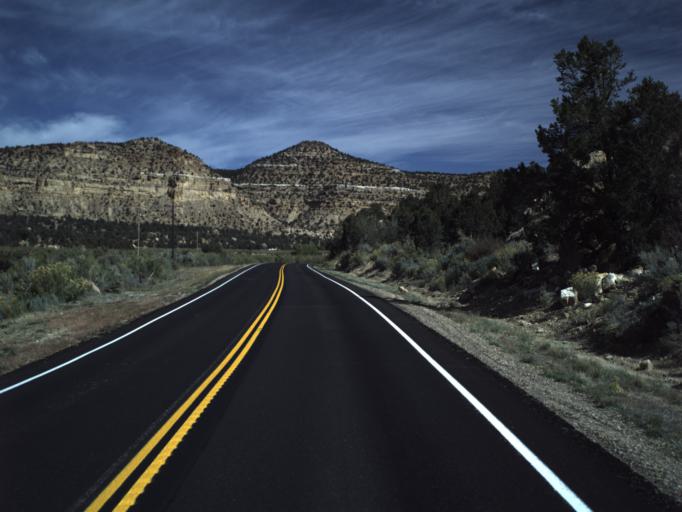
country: US
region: Utah
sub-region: Wayne County
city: Loa
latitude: 37.7521
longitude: -111.7021
